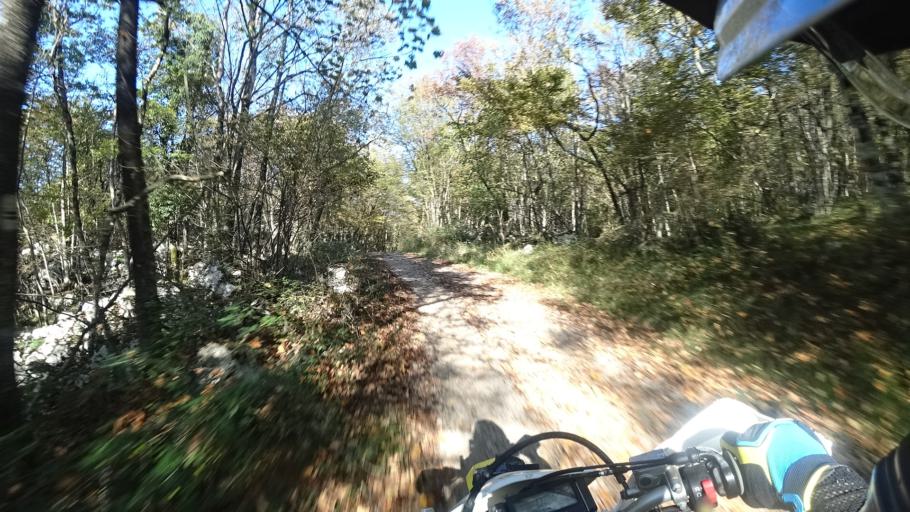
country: HR
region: Primorsko-Goranska
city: Kastav
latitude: 45.4107
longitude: 14.3384
